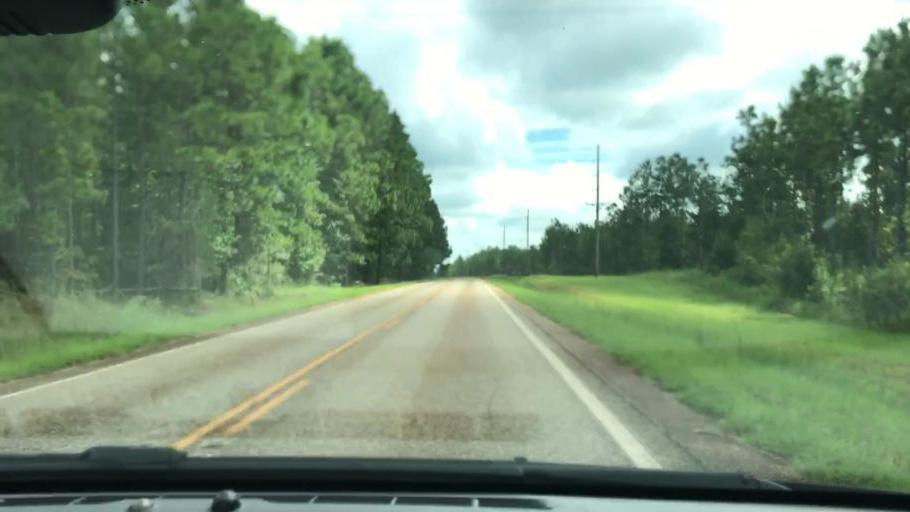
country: US
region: Georgia
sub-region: Stewart County
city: Lumpkin
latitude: 32.0663
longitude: -84.8946
